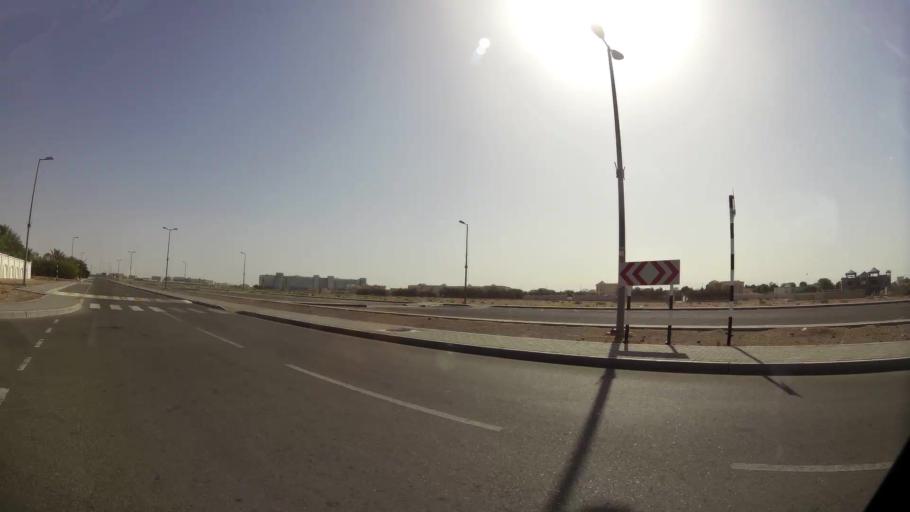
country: OM
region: Al Buraimi
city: Al Buraymi
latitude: 24.3391
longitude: 55.7881
